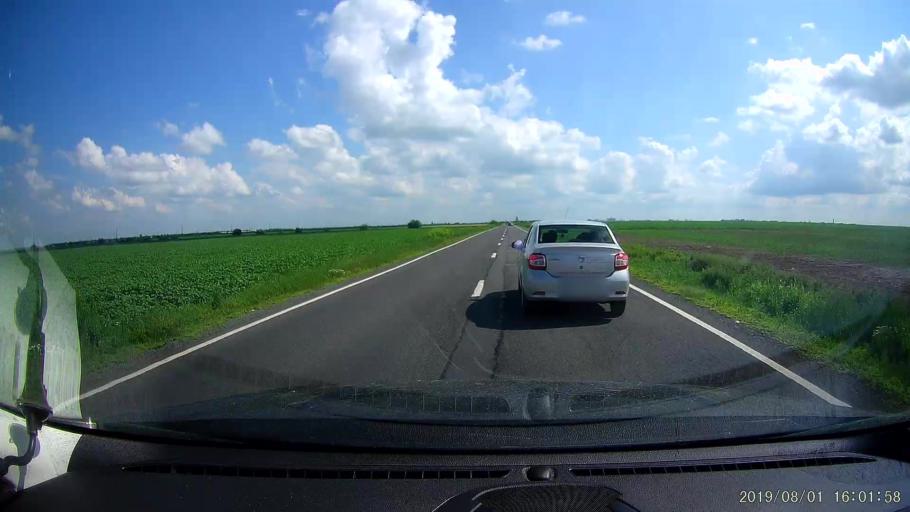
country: RO
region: Ialomita
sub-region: Comuna Ciulnita
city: Ciulnita
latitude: 44.4989
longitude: 27.3889
